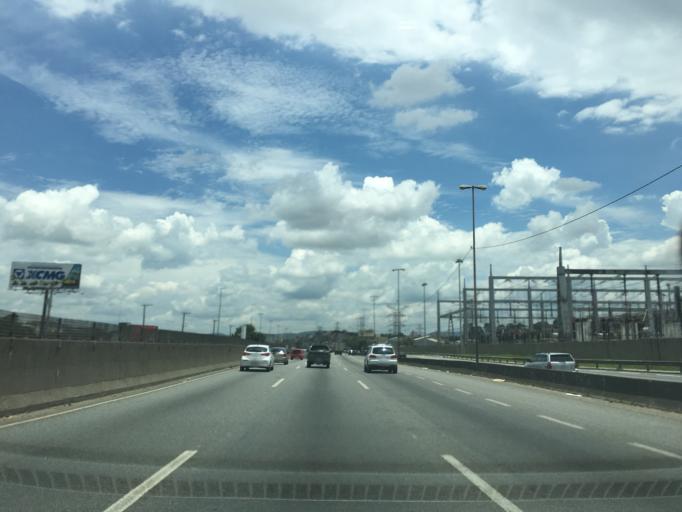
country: BR
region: Sao Paulo
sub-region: Guarulhos
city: Guarulhos
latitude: -23.4841
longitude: -46.5597
